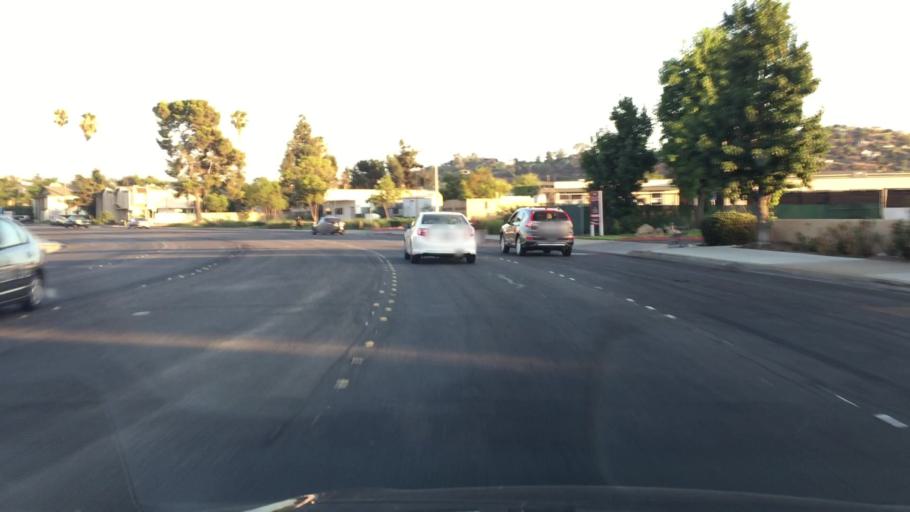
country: US
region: California
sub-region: San Diego County
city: Bostonia
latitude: 32.7947
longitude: -116.9358
